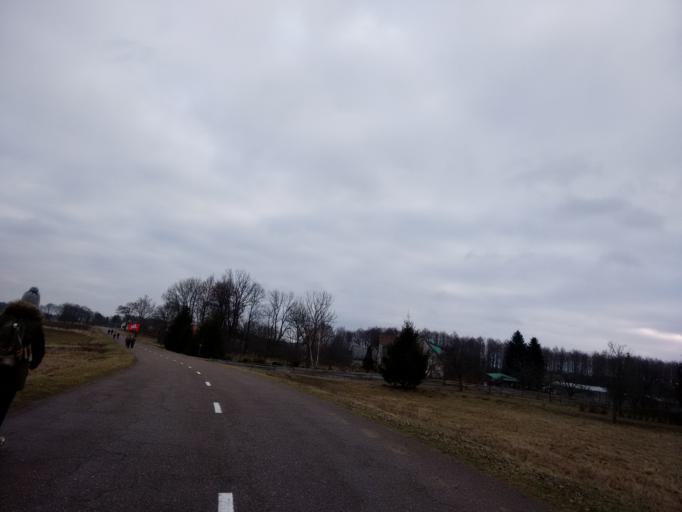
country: LT
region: Alytaus apskritis
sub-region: Alytus
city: Alytus
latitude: 54.2445
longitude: 23.9079
